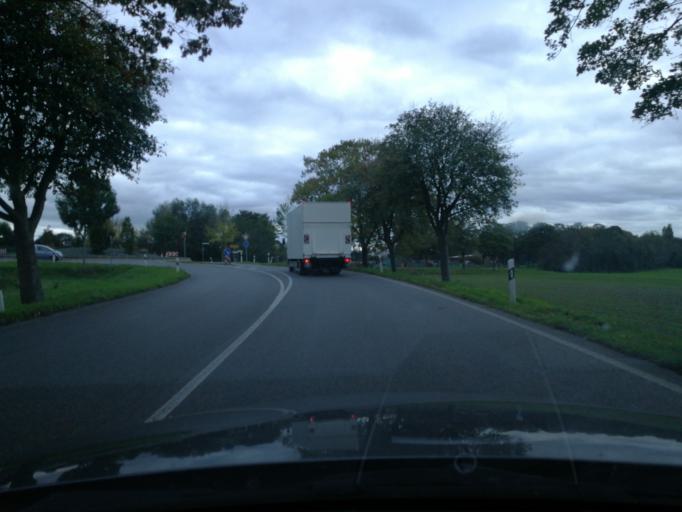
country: DE
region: North Rhine-Westphalia
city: Straelen
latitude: 51.4259
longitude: 6.2426
